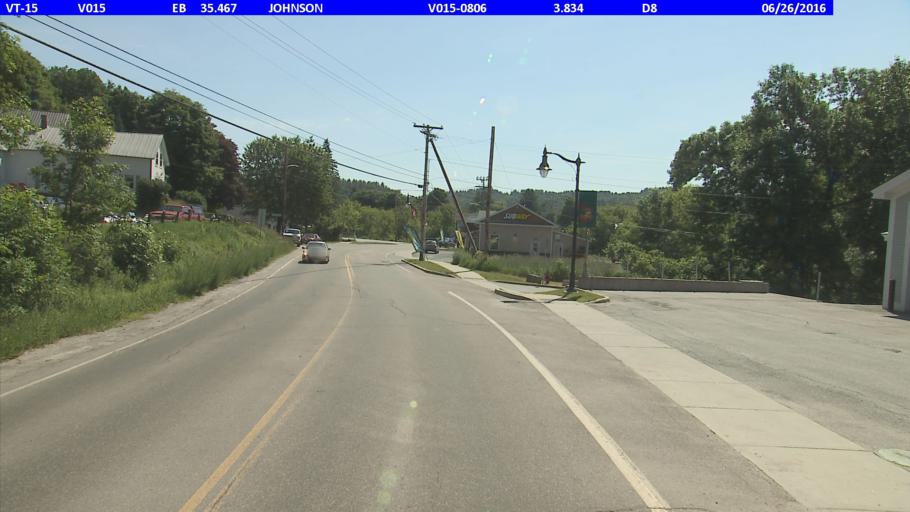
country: US
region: Vermont
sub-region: Lamoille County
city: Johnson
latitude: 44.6364
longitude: -72.6841
